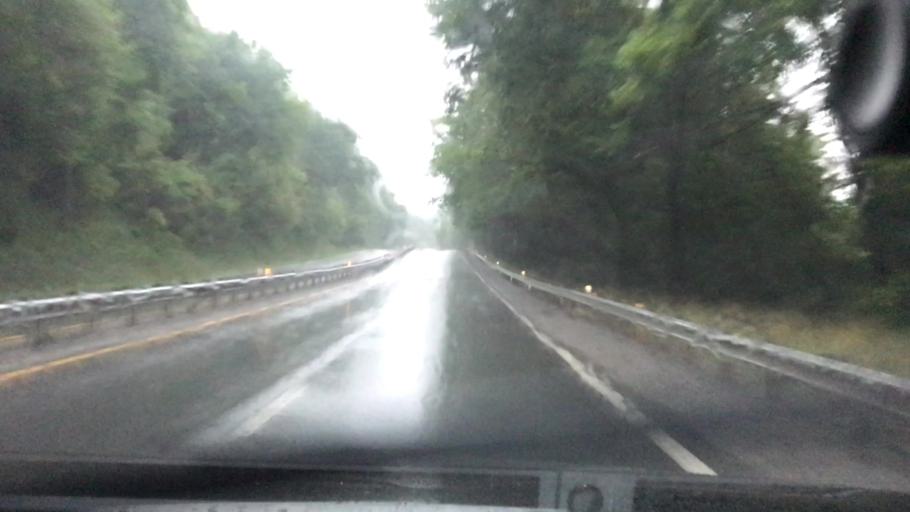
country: US
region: Virginia
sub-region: Giles County
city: Narrows
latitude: 37.3459
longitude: -80.7836
